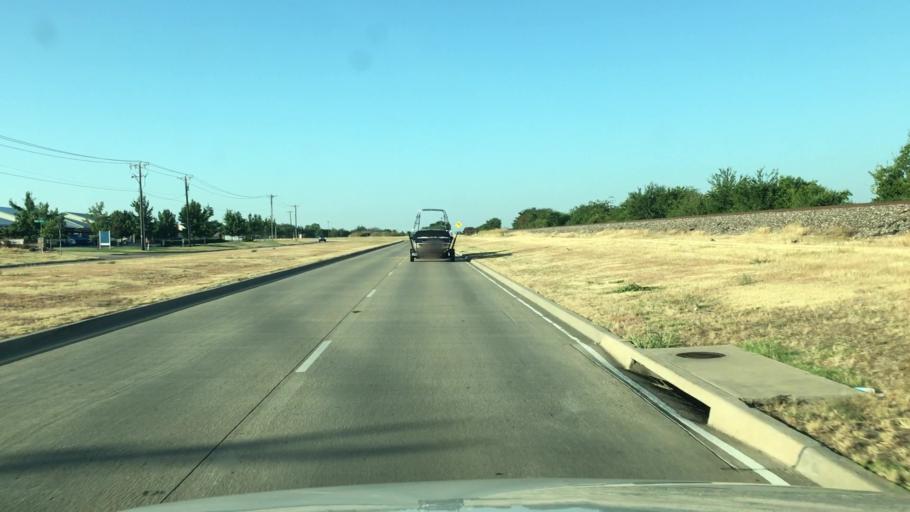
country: US
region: Texas
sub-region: Tarrant County
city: Crowley
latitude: 32.5482
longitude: -97.3655
